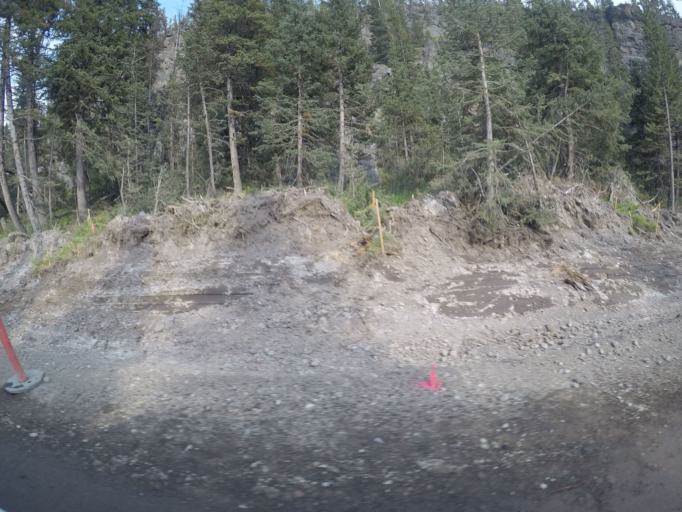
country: US
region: Montana
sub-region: Gallatin County
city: West Yellowstone
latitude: 44.8227
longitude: -110.7284
